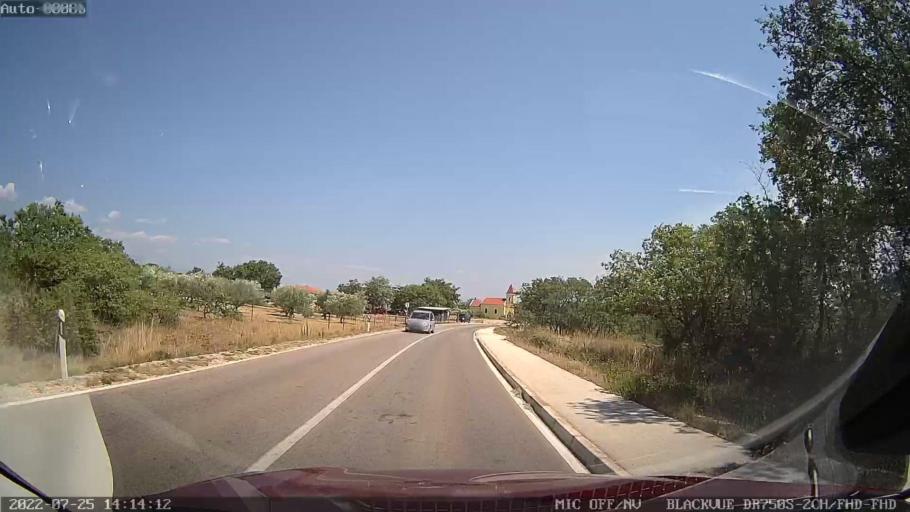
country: HR
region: Zadarska
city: Vrsi
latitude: 44.2063
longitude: 15.2477
